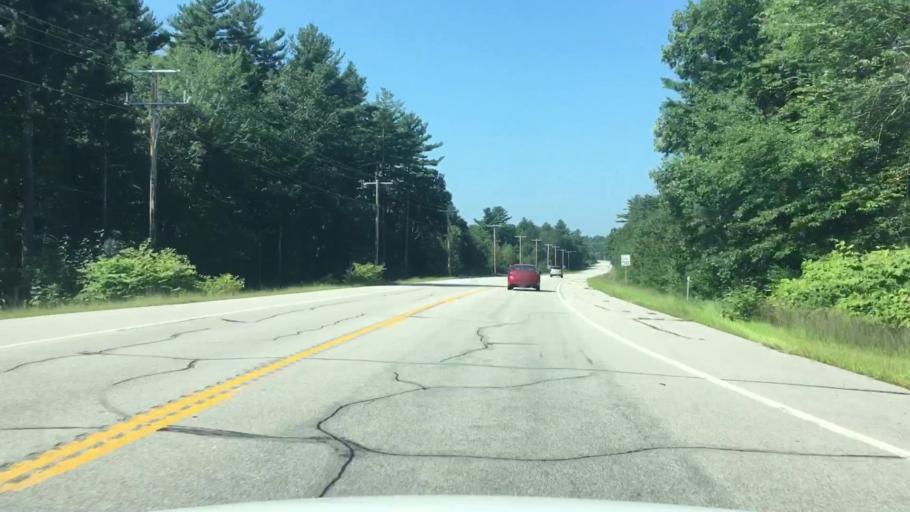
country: US
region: New Hampshire
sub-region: Rockingham County
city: Danville
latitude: 42.9086
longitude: -71.0871
